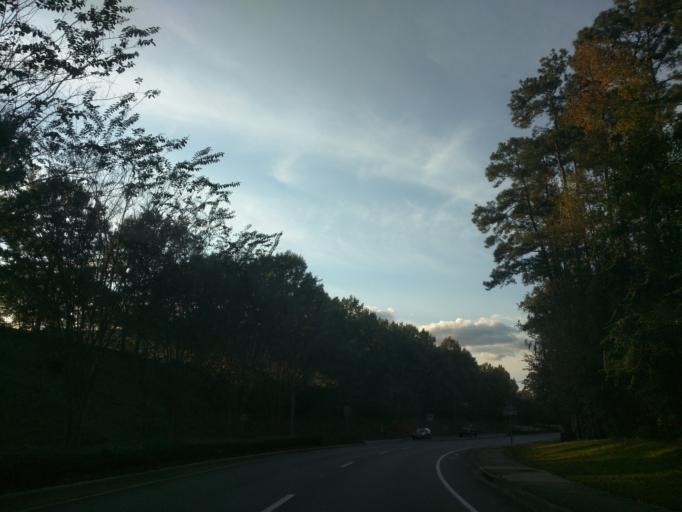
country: US
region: Florida
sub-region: Leon County
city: Tallahassee
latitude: 30.4379
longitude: -84.2506
